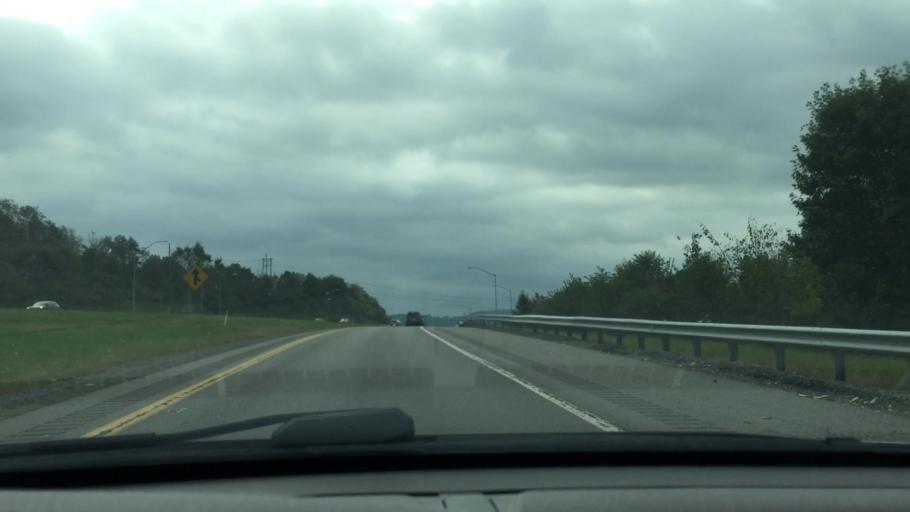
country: US
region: Pennsylvania
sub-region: Washington County
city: Muse
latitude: 40.2956
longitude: -80.1691
